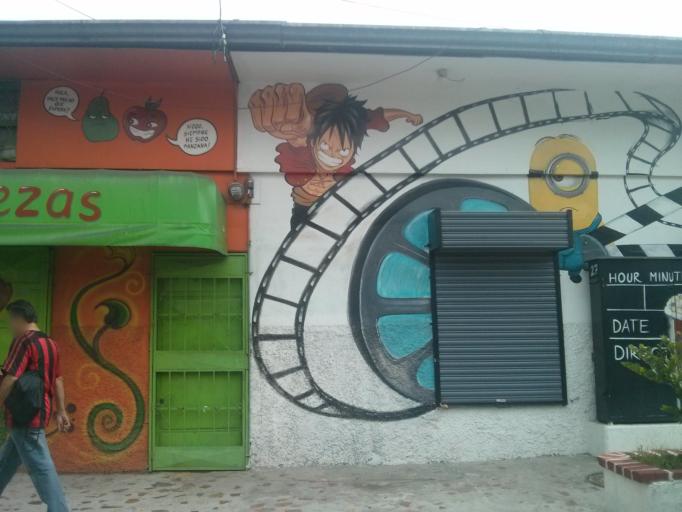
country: CR
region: San Jose
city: Colima
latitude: 9.9474
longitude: -84.0885
